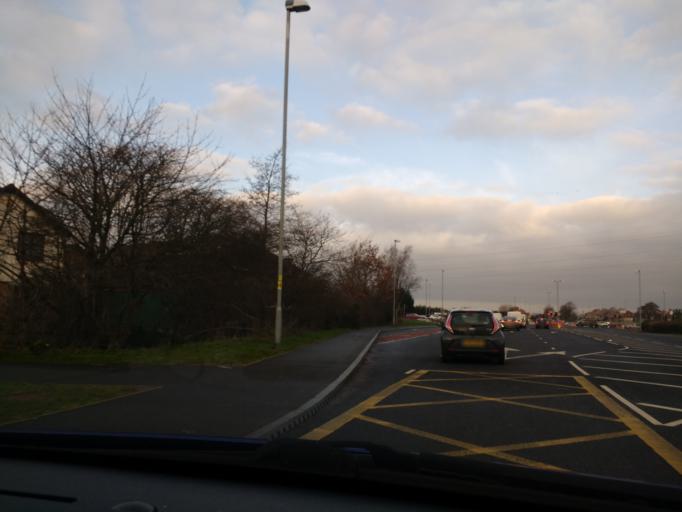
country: GB
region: England
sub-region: Lancashire
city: Lancaster
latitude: 54.0614
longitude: -2.8284
